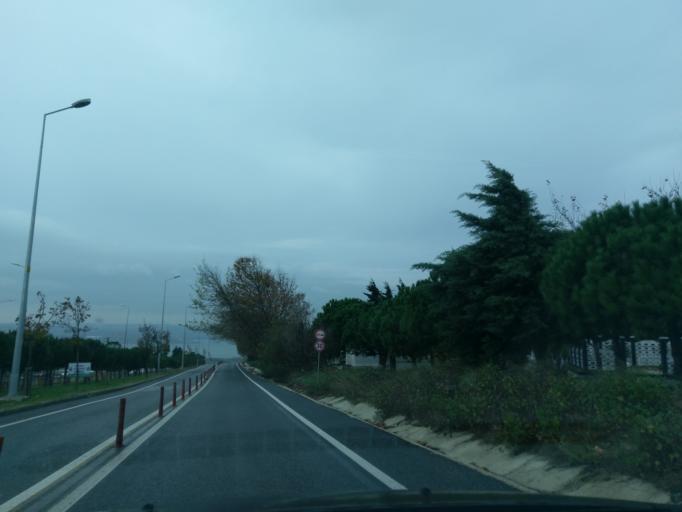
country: TR
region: Istanbul
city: Bueyuekcekmece
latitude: 41.0263
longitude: 28.6123
